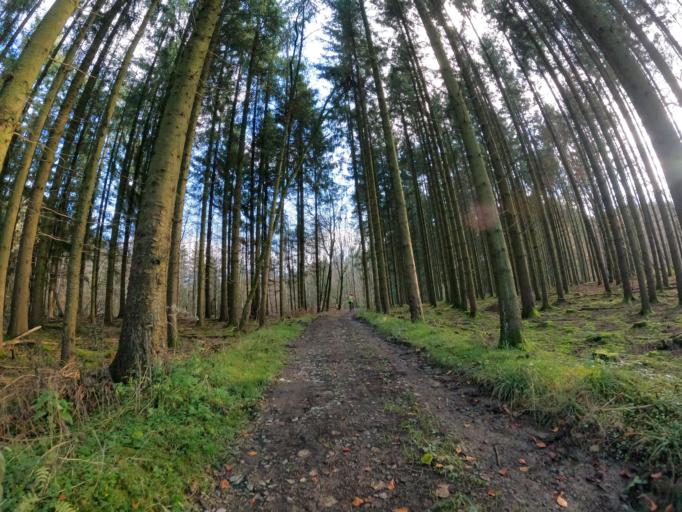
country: LU
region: Diekirch
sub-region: Canton de Wiltz
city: Winseler
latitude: 49.9861
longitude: 5.8418
